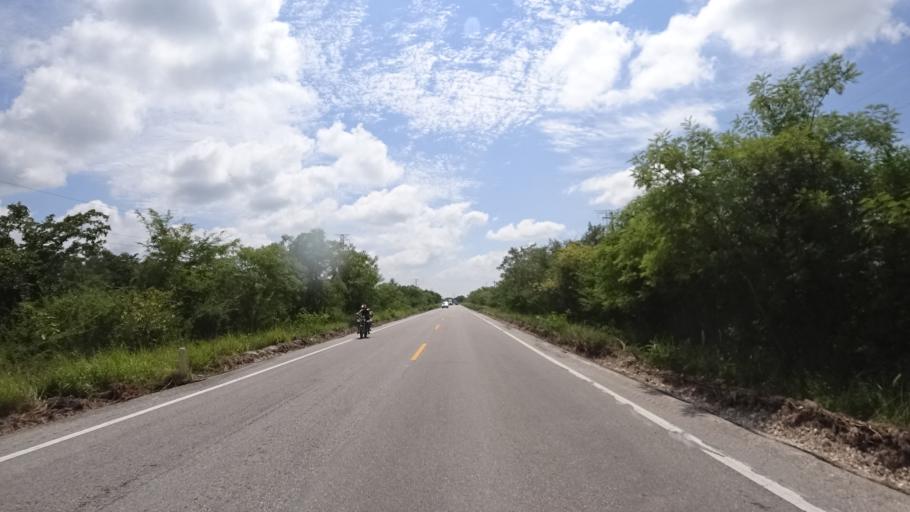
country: MX
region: Campeche
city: Sabancuy
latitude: 18.9447
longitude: -91.1296
